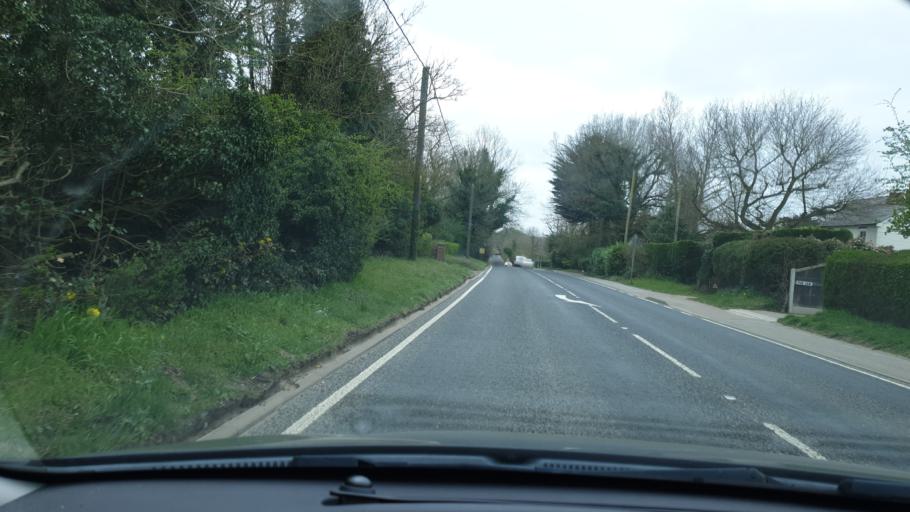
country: GB
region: England
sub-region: Essex
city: Great Horkesley
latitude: 51.9258
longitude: 0.8813
